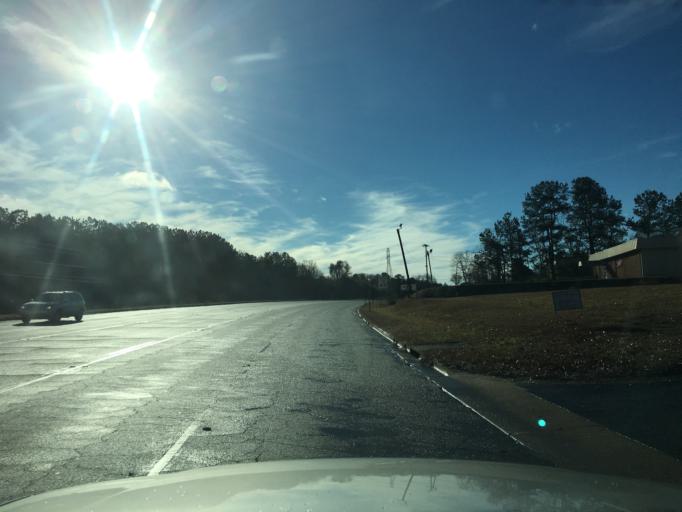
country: US
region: South Carolina
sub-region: Spartanburg County
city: Mayo
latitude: 35.0233
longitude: -81.8742
